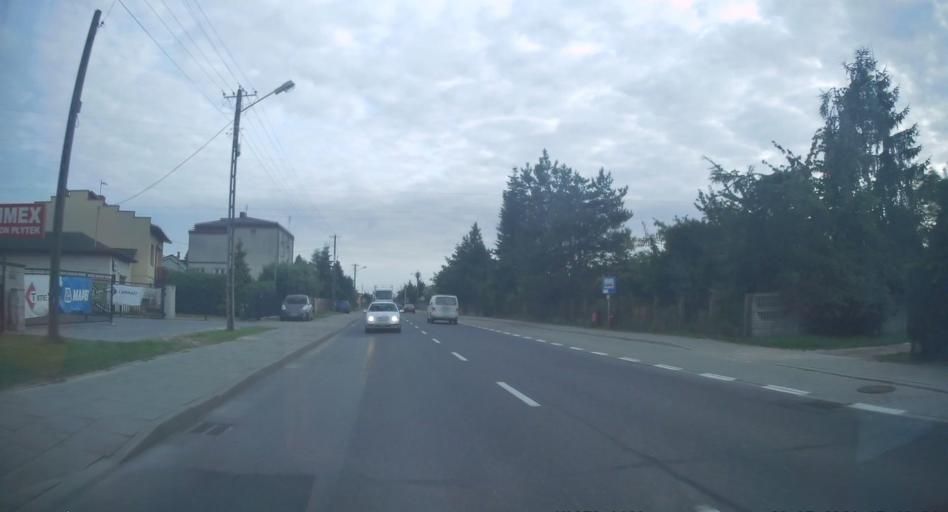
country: PL
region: Lodz Voivodeship
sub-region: Powiat radomszczanski
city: Radomsko
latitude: 51.0898
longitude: 19.4561
